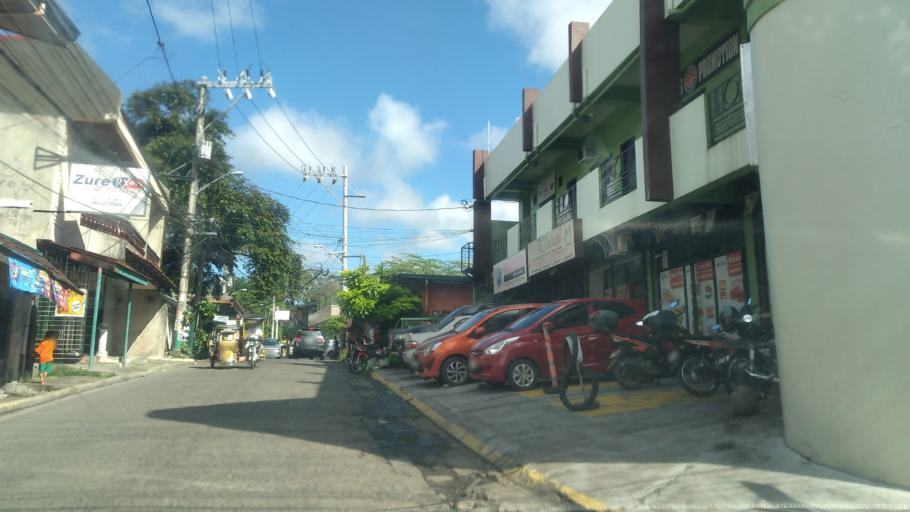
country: PH
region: Calabarzon
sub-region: Province of Quezon
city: Lucena
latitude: 13.9399
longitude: 121.6119
